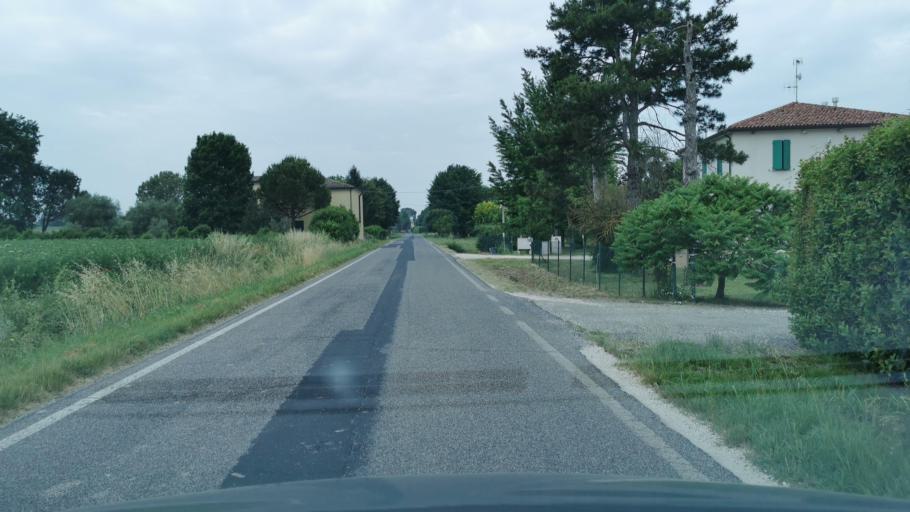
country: IT
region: Emilia-Romagna
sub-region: Provincia di Ravenna
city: Russi
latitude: 44.3826
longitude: 11.9975
